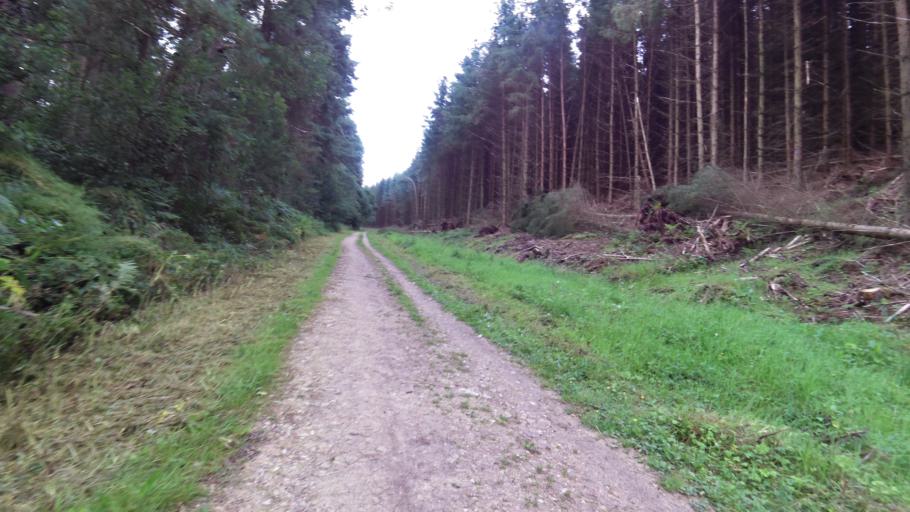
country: GB
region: England
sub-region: North Yorkshire
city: Thornton Dale
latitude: 54.2839
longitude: -0.6768
